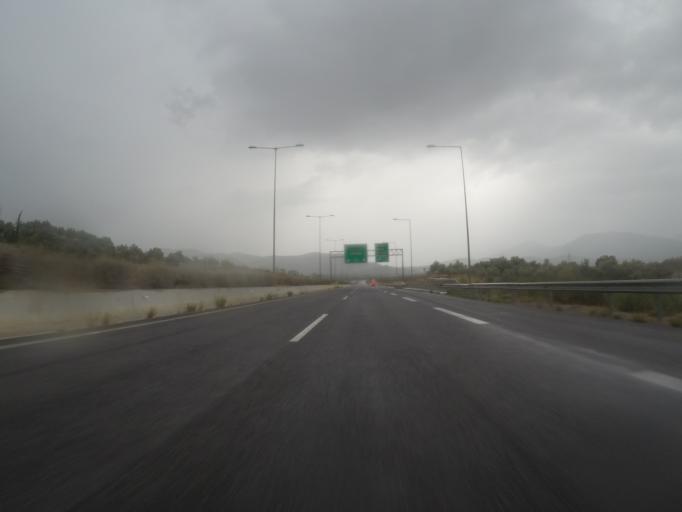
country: GR
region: Peloponnese
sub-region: Nomos Messinias
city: Meligalas
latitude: 37.2559
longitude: 22.0242
